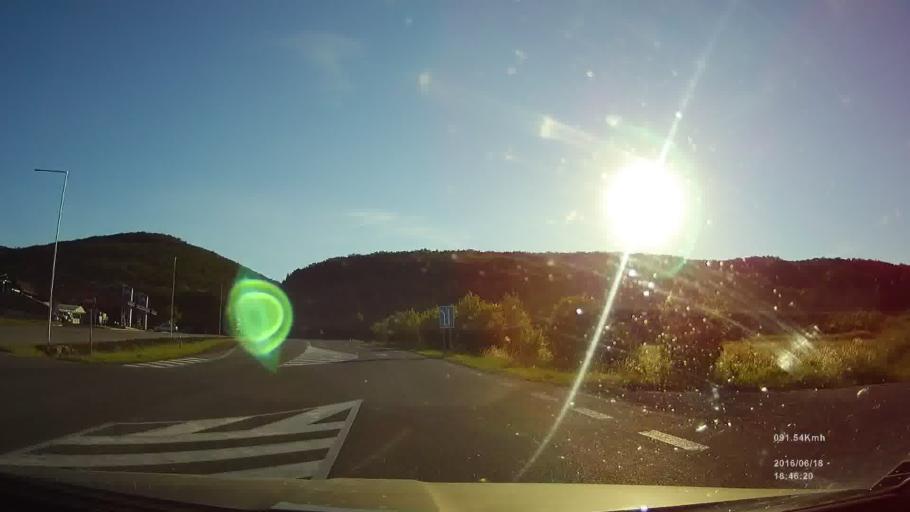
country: SK
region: Kosicky
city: Secovce
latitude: 48.7359
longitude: 21.5672
